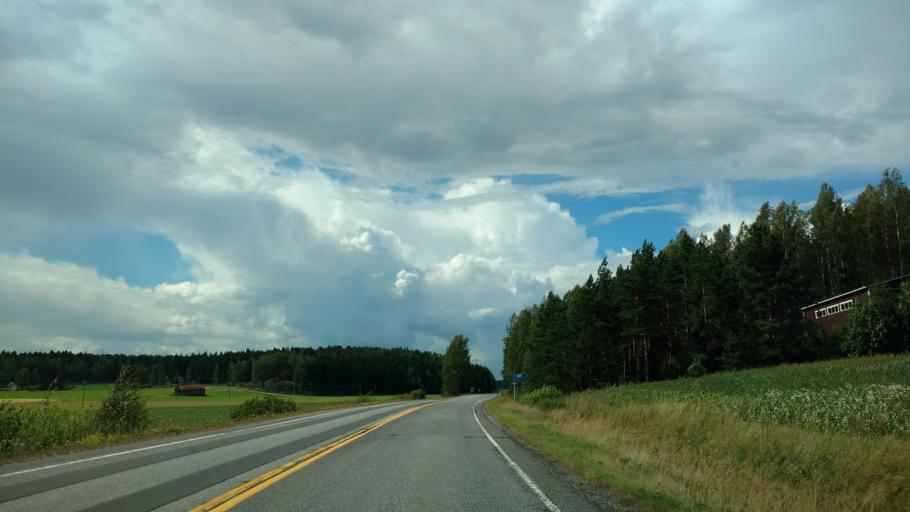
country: FI
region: Varsinais-Suomi
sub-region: Salo
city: Halikko
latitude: 60.3833
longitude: 22.8915
